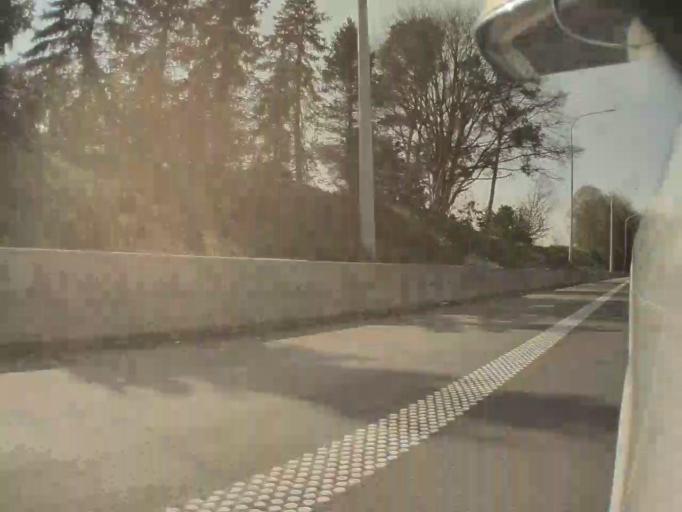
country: BE
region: Wallonia
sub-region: Province de Namur
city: Hamois
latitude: 50.2898
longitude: 5.1765
